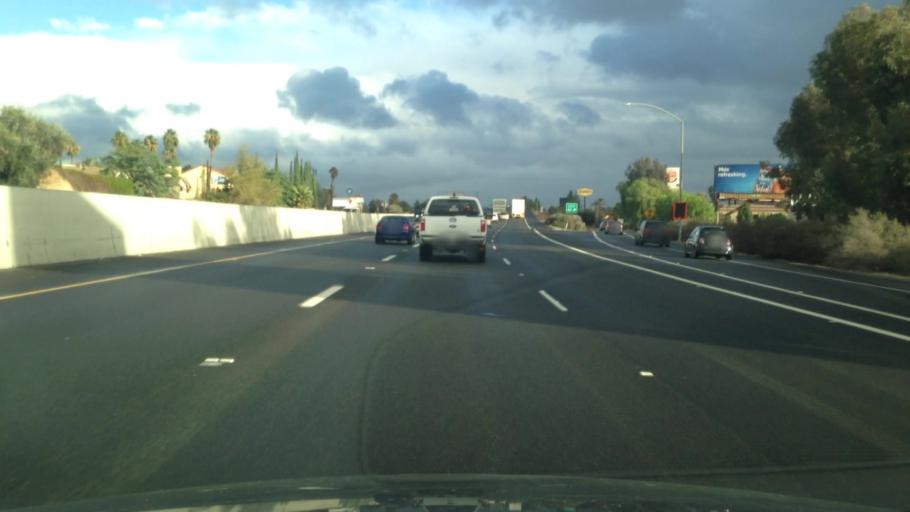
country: US
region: California
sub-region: Riverside County
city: Moreno Valley
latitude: 33.9409
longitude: -117.2321
